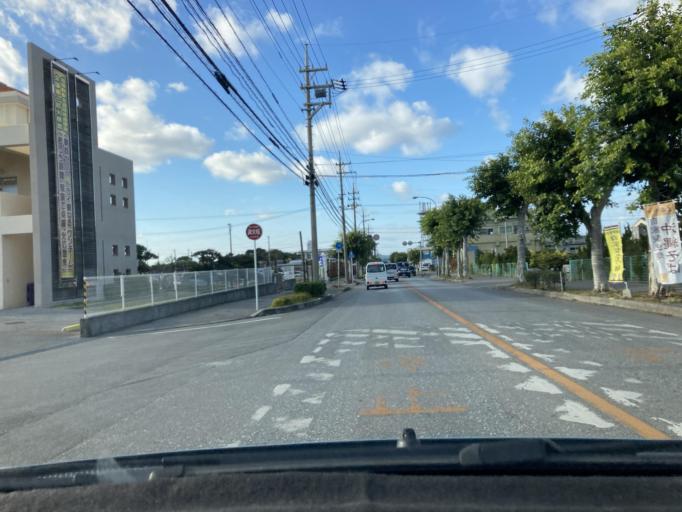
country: JP
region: Okinawa
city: Gushikawa
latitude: 26.3603
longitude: 127.8616
